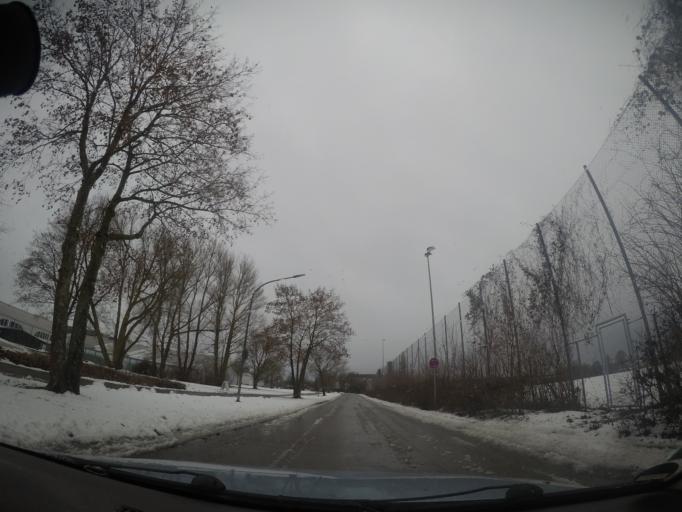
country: DE
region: Bavaria
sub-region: Swabia
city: Neu-Ulm
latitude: 48.3804
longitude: 10.0038
